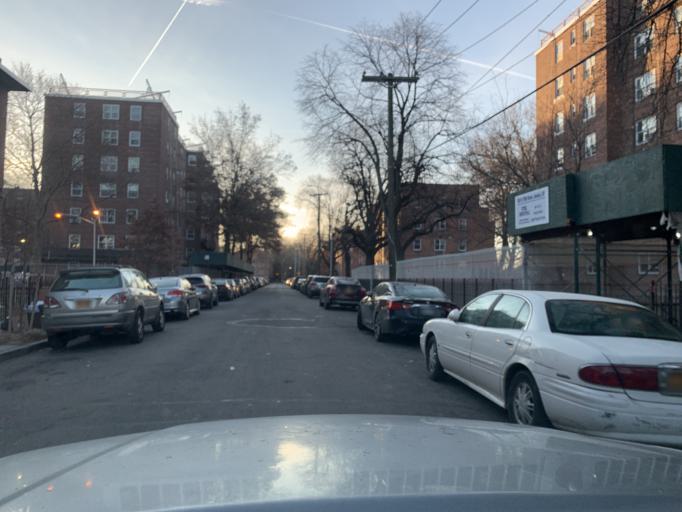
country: US
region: New York
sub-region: Queens County
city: Jamaica
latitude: 40.6984
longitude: -73.7963
